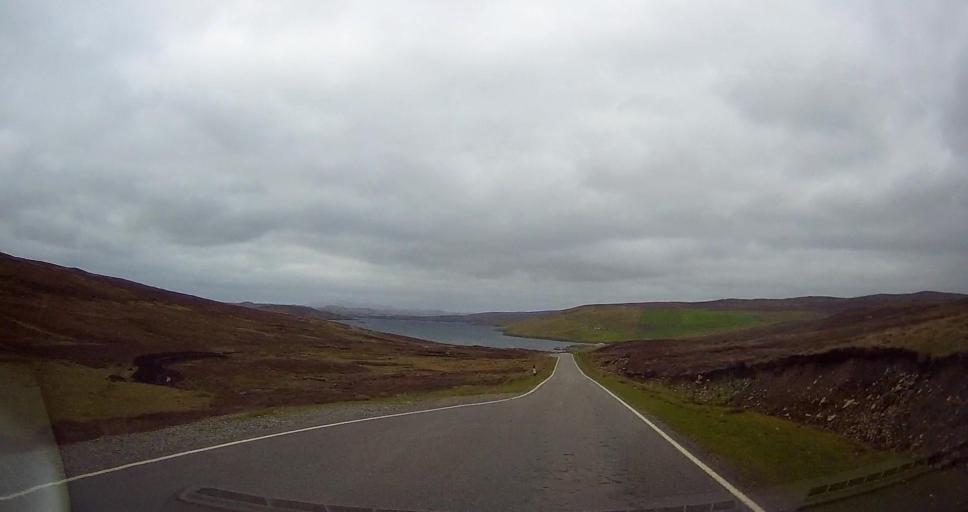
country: GB
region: Scotland
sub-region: Shetland Islands
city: Lerwick
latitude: 60.3258
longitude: -1.3389
